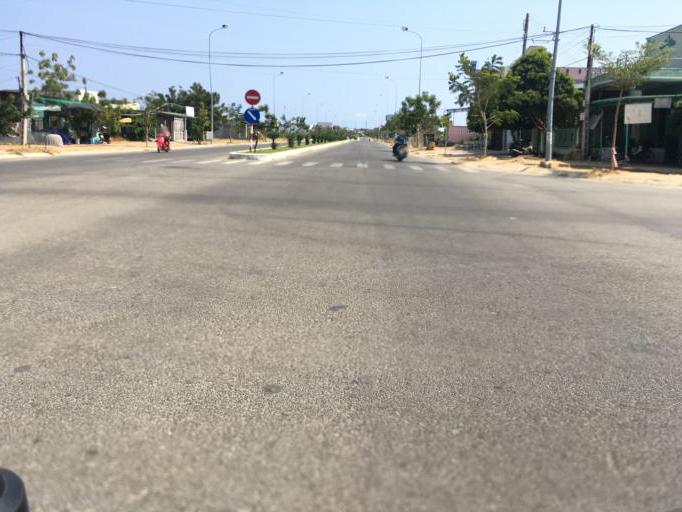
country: VN
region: Ninh Thuan
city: Phan Rang-Thap Cham
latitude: 11.5583
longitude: 109.0216
